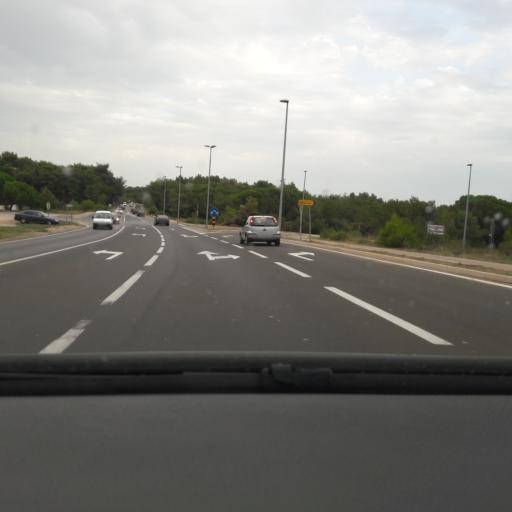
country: HR
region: Zadarska
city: Zadar
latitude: 44.1543
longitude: 15.2151
